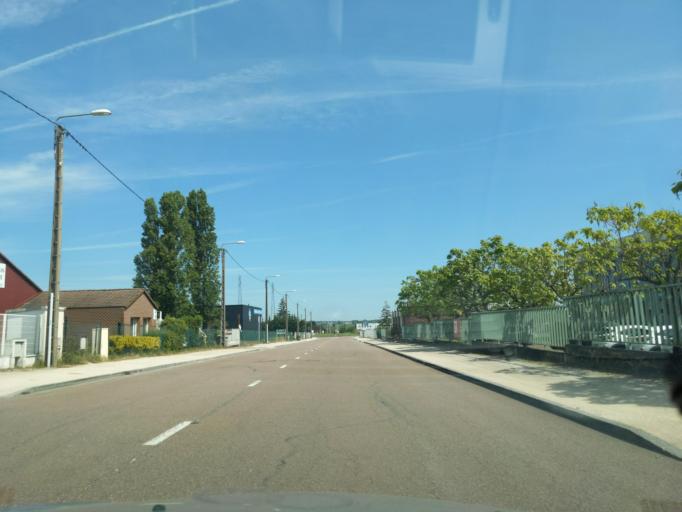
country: FR
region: Bourgogne
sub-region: Departement de la Cote-d'Or
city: Saint-Apollinaire
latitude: 47.3467
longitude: 5.0723
